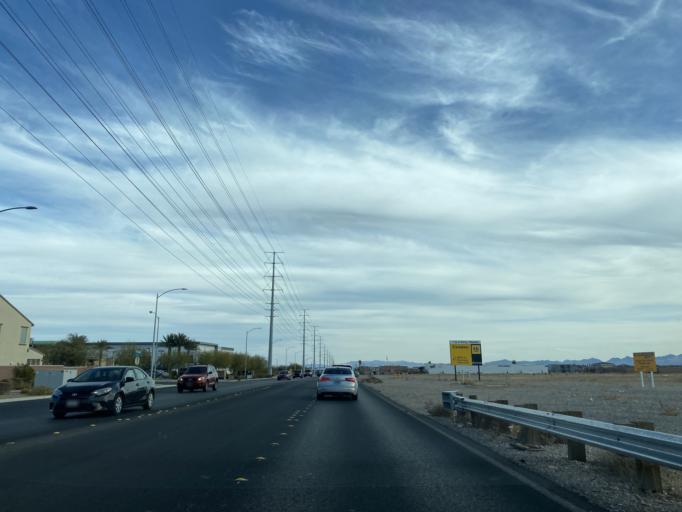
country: US
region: Nevada
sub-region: Clark County
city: Enterprise
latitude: 36.0555
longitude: -115.2665
